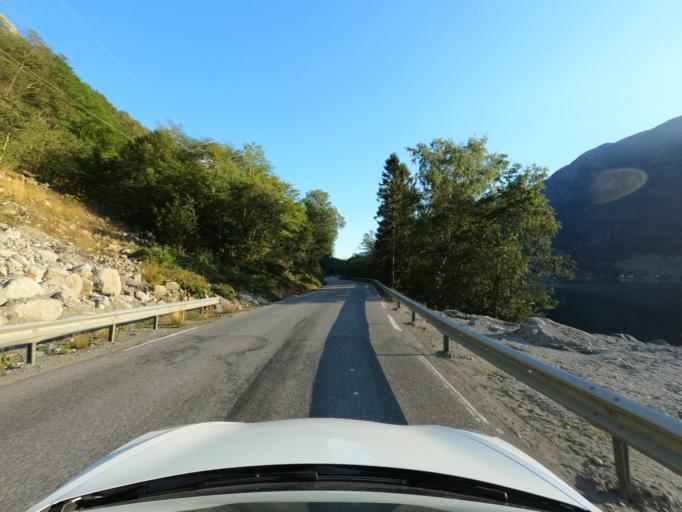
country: NO
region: Hordaland
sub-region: Odda
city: Odda
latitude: 60.0877
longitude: 6.5500
